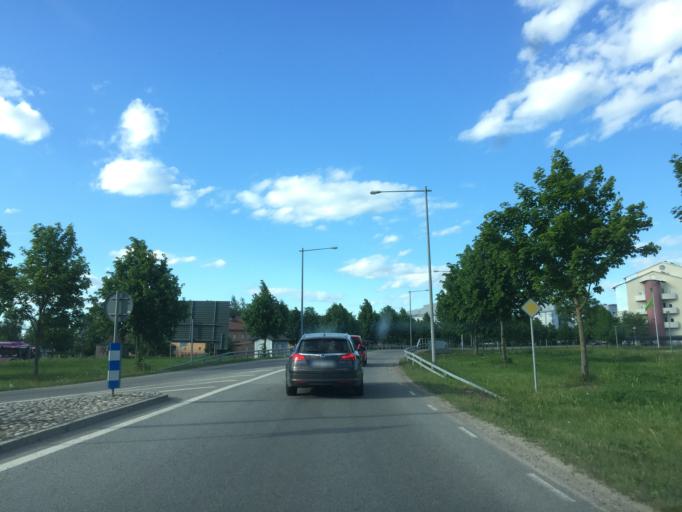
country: SE
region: OErebro
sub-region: Orebro Kommun
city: Orebro
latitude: 59.2530
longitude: 15.2364
